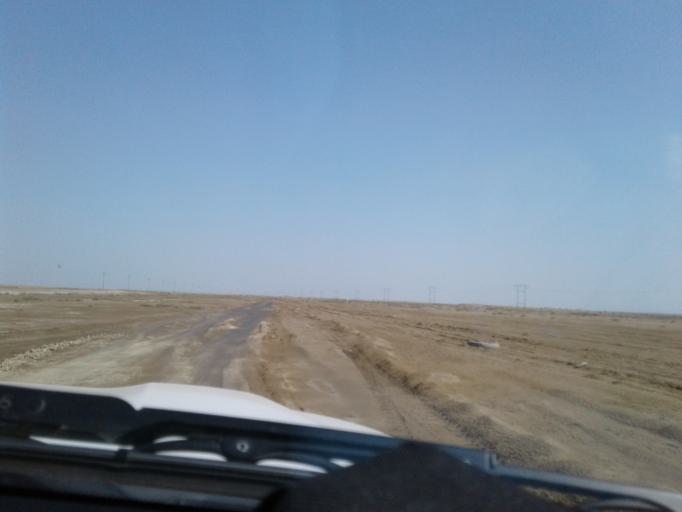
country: IR
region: Golestan
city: Gomishan
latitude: 37.7943
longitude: 53.9182
